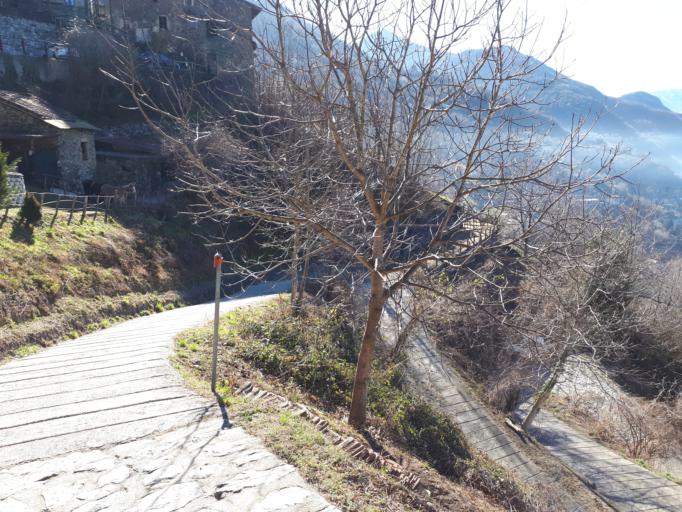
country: IT
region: Lombardy
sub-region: Provincia di Lecco
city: Bellano
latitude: 46.0587
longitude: 9.3161
